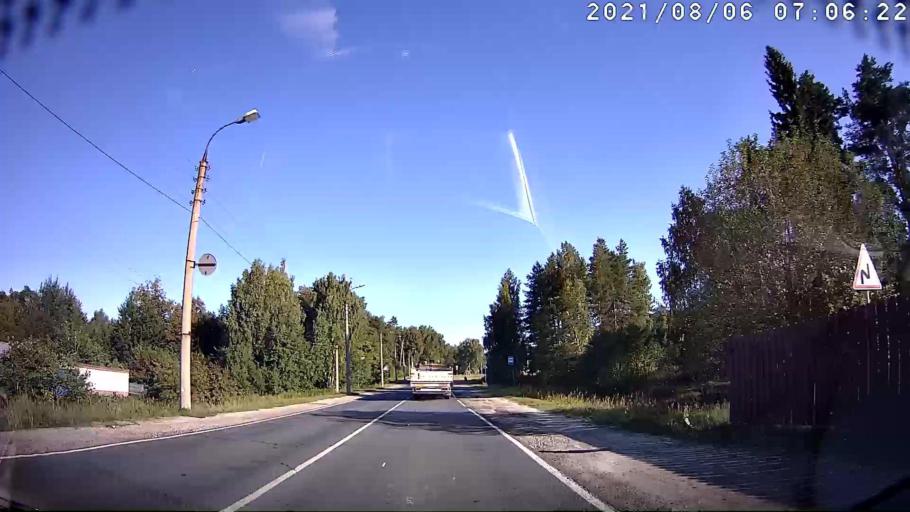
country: RU
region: Mariy-El
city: Yoshkar-Ola
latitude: 56.5584
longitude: 47.9815
